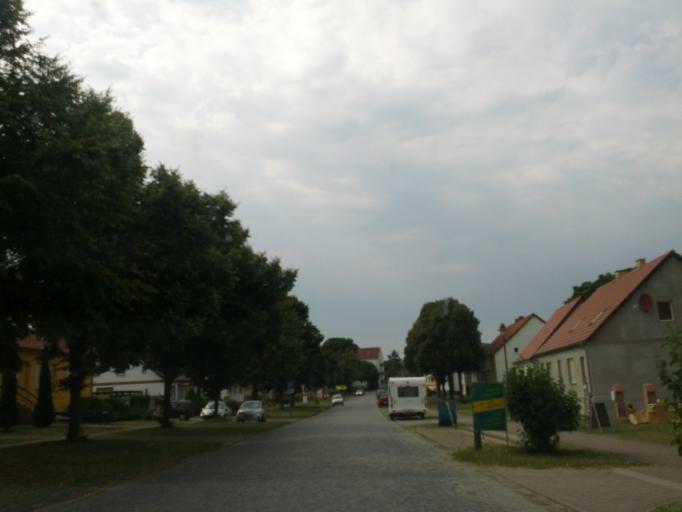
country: DE
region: Brandenburg
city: Fehrbellin
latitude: 52.7588
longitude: 12.8781
